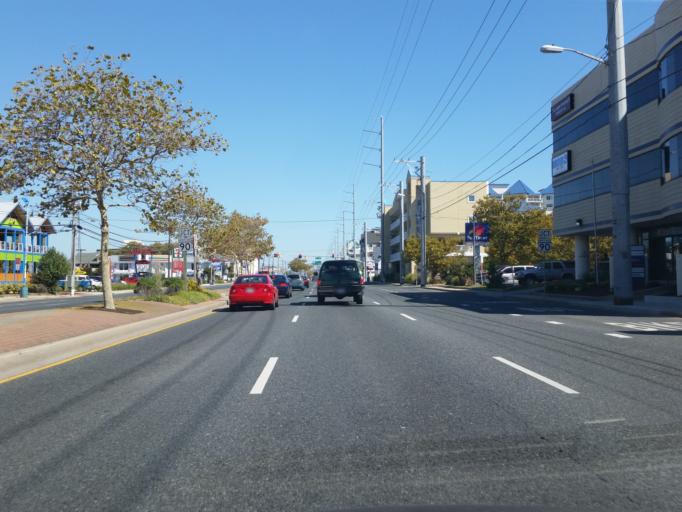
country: US
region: Maryland
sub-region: Worcester County
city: Ocean City
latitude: 38.3812
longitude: -75.0676
